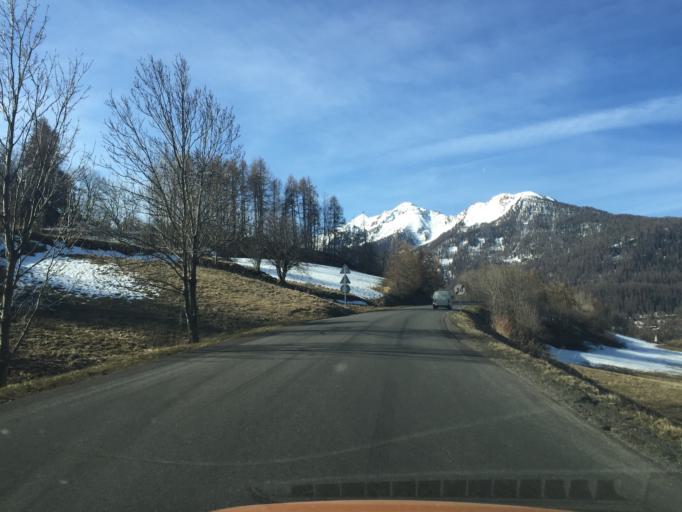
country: FR
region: Provence-Alpes-Cote d'Azur
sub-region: Departement des Hautes-Alpes
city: Embrun
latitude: 44.5078
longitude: 6.5582
